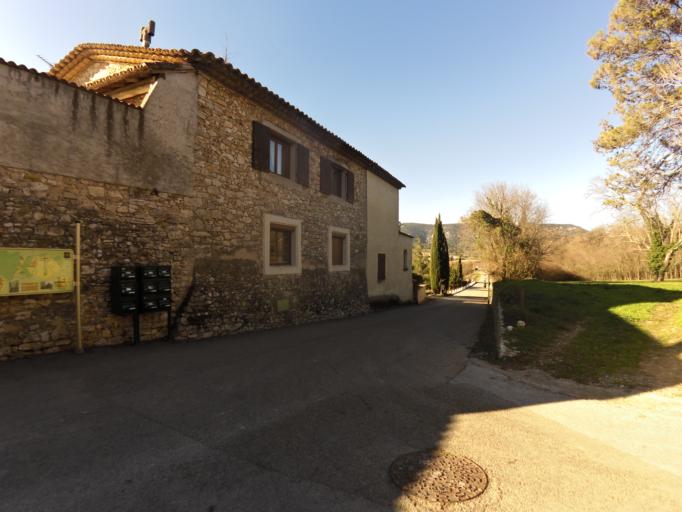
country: FR
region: Languedoc-Roussillon
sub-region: Departement du Gard
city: Quissac
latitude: 43.8935
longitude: 3.9987
